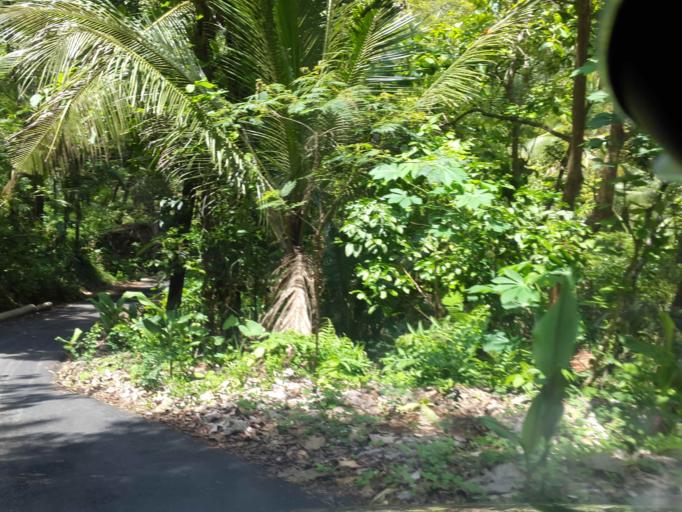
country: ID
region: Central Java
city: Kutoarjo
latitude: -7.7556
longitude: 110.0743
